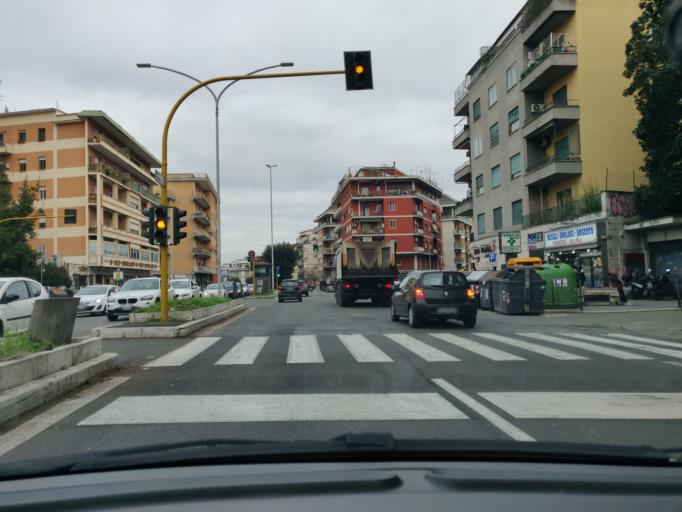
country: VA
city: Vatican City
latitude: 41.8985
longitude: 12.4291
